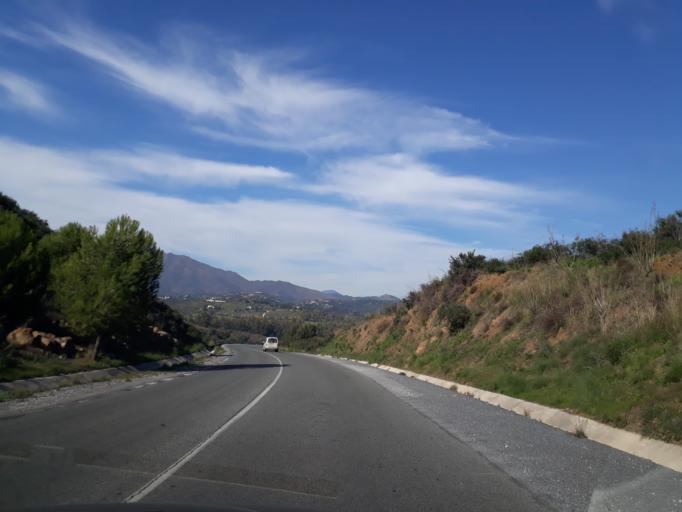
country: ES
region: Andalusia
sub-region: Provincia de Malaga
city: Fuengirola
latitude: 36.5367
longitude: -4.6863
